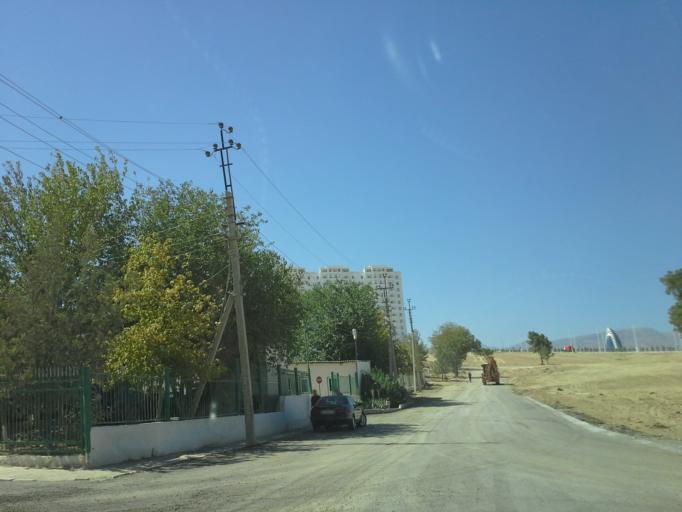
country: TM
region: Ahal
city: Ashgabat
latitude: 37.9466
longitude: 58.3472
